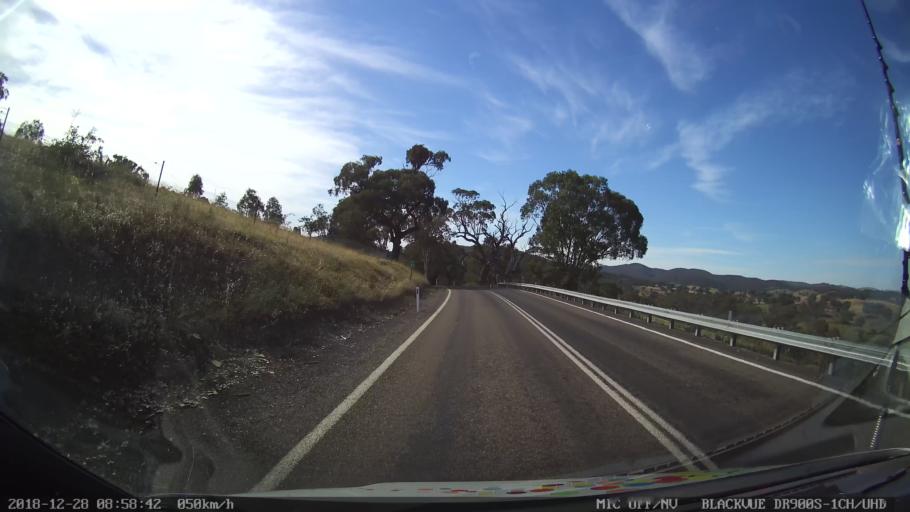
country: AU
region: New South Wales
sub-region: Upper Lachlan Shire
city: Crookwell
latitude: -34.1291
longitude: 149.3322
